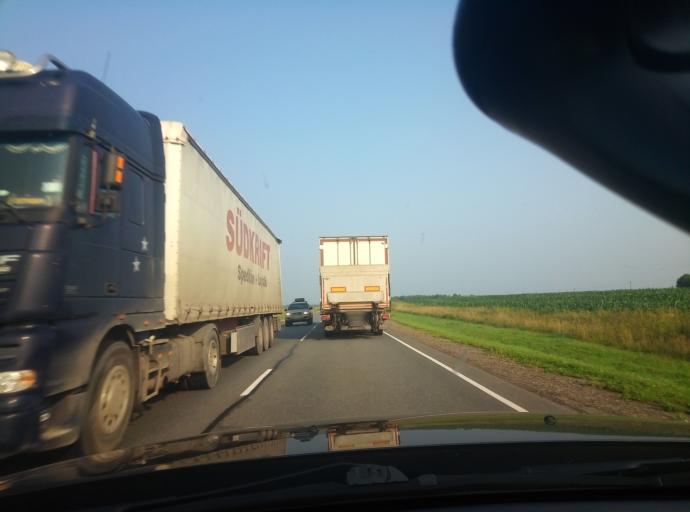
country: RU
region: Tula
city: Khanino
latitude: 54.4014
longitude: 36.5780
